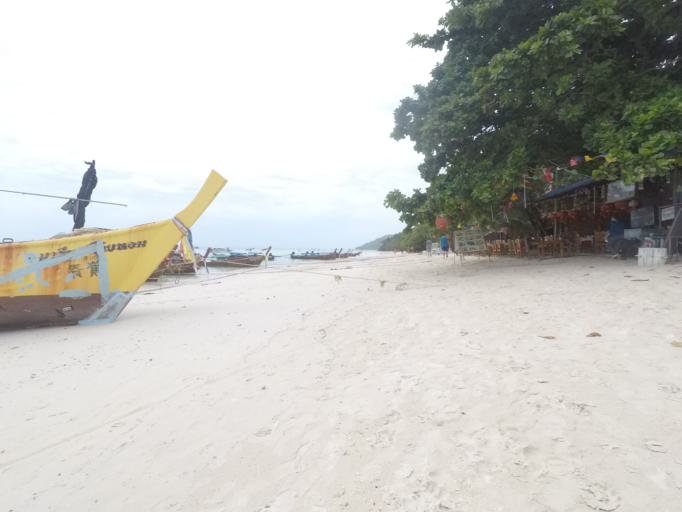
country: TH
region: Phangnga
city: Ban Phru Nai
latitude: 7.7774
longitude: 98.7630
